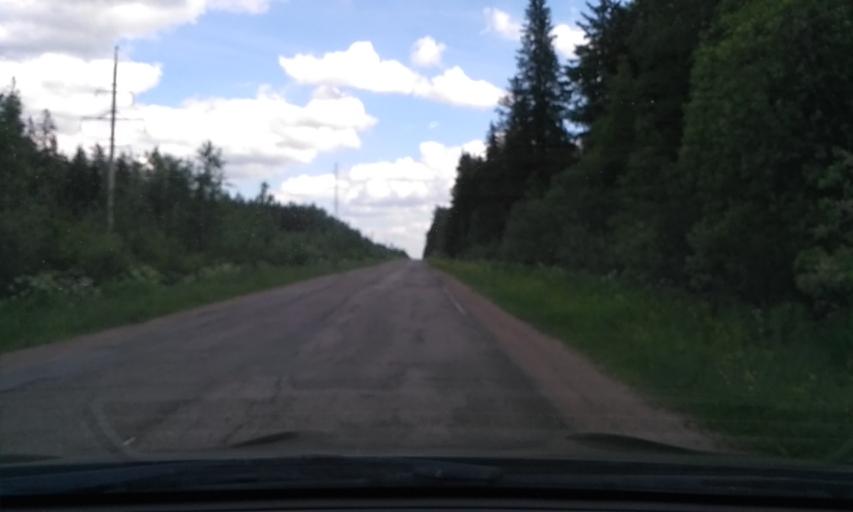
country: RU
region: Leningrad
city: Otradnoye
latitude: 59.8219
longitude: 30.7664
